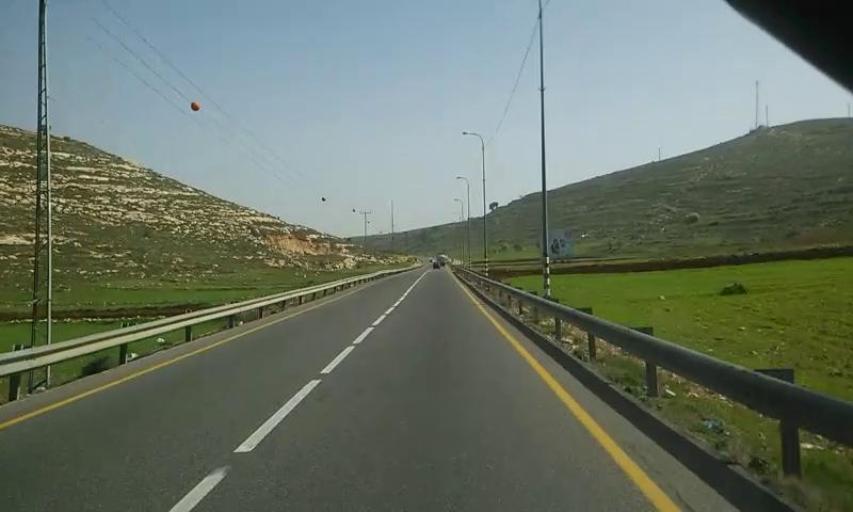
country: PS
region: West Bank
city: Sinjil
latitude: 32.0248
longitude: 35.2733
